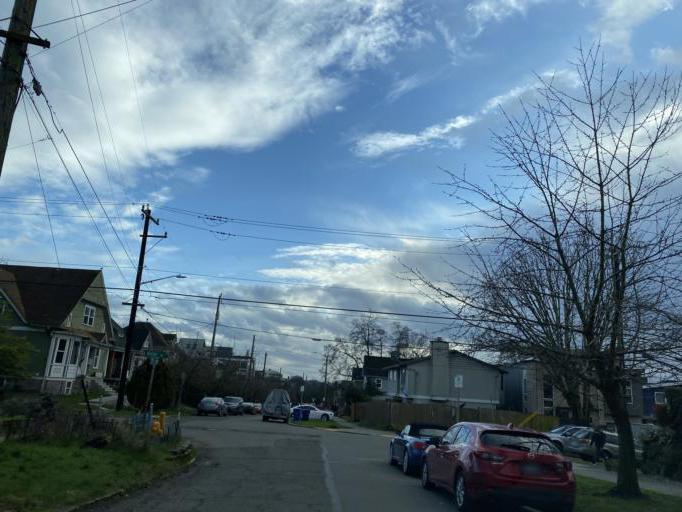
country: US
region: Washington
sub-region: King County
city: Seattle
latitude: 47.6046
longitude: -122.3103
